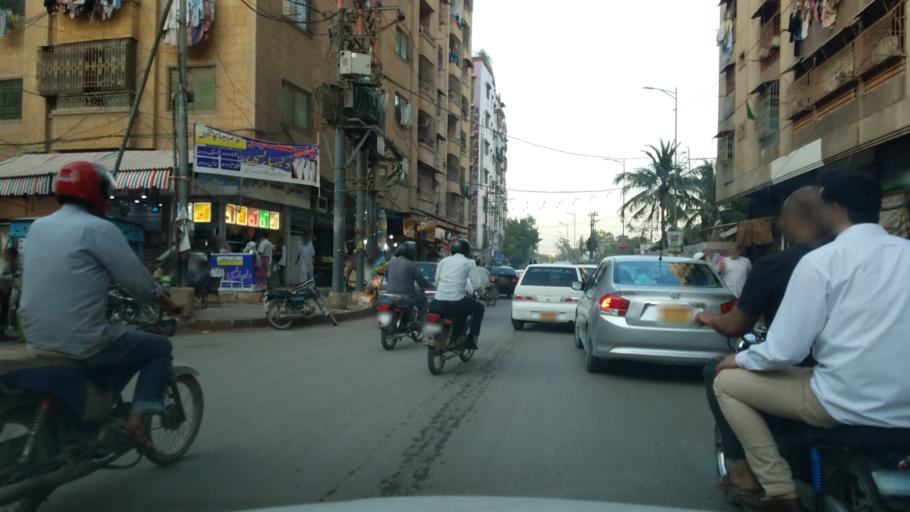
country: PK
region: Sindh
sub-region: Karachi District
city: Karachi
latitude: 24.8791
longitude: 67.0204
